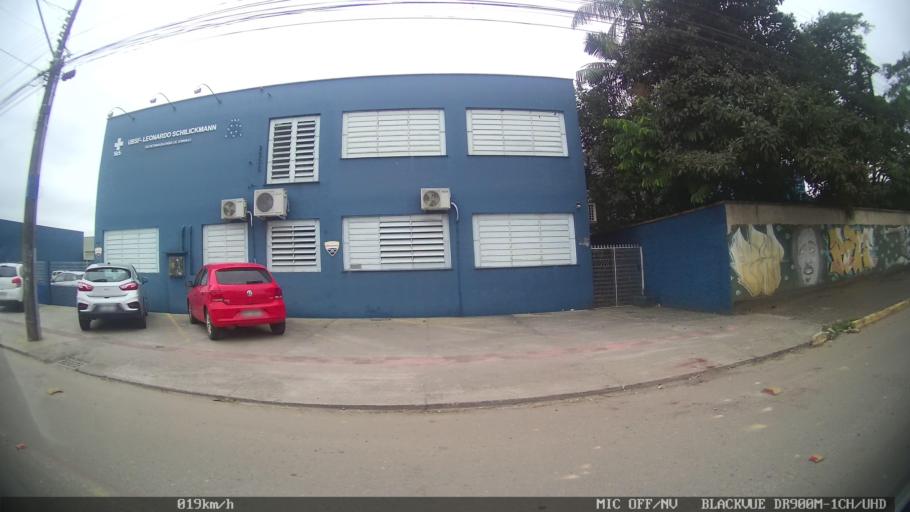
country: BR
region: Santa Catarina
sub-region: Joinville
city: Joinville
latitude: -26.2728
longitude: -48.8253
